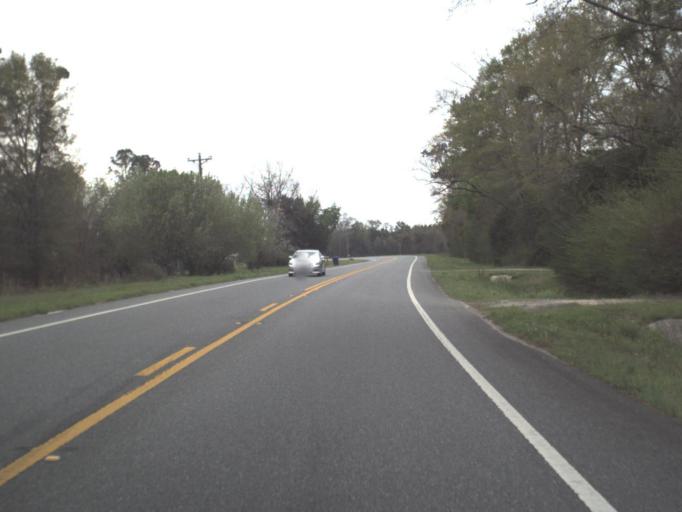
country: US
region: Florida
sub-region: Calhoun County
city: Blountstown
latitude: 30.4709
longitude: -85.1983
